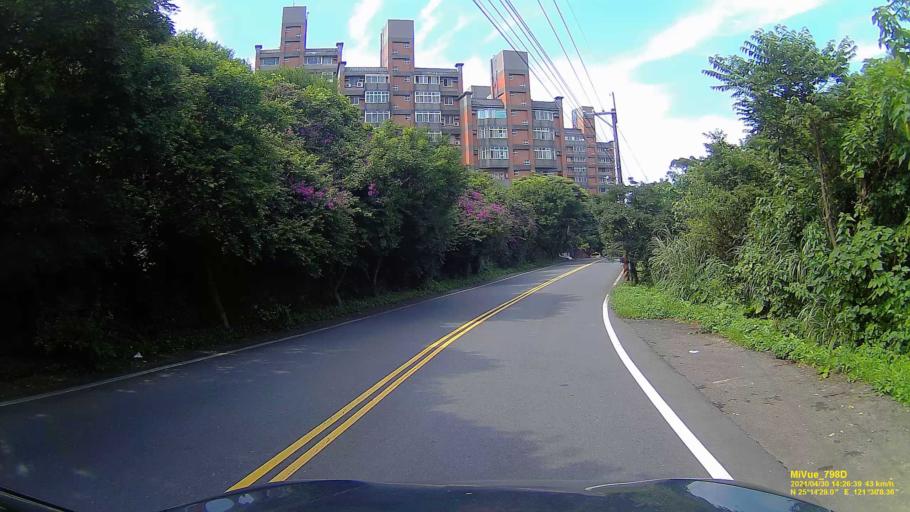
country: TW
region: Taipei
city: Taipei
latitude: 25.2417
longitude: 121.5023
